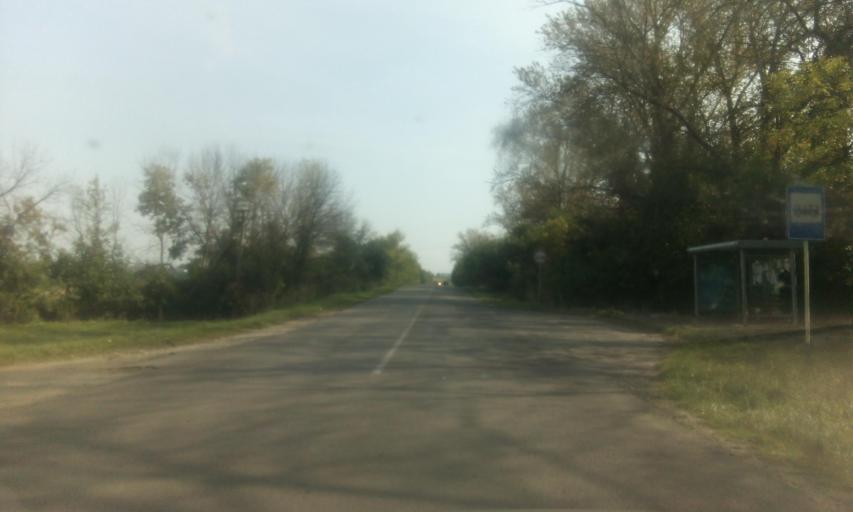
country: RU
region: Tula
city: Partizan
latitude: 53.9737
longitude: 38.1281
